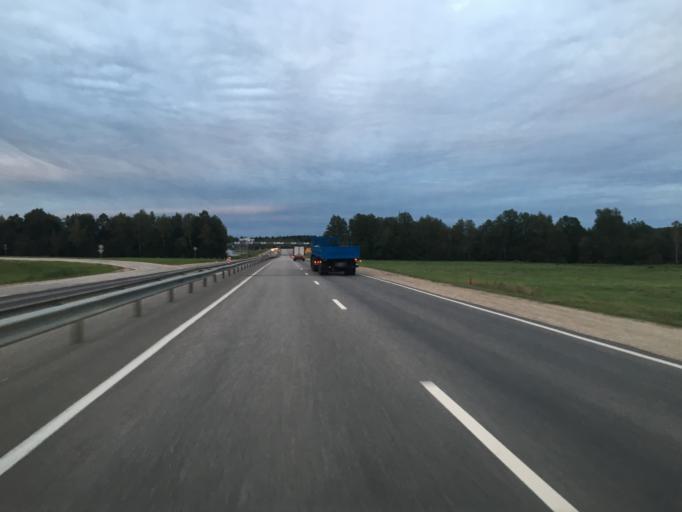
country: RU
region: Kaluga
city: Detchino
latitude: 54.6738
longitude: 36.2921
